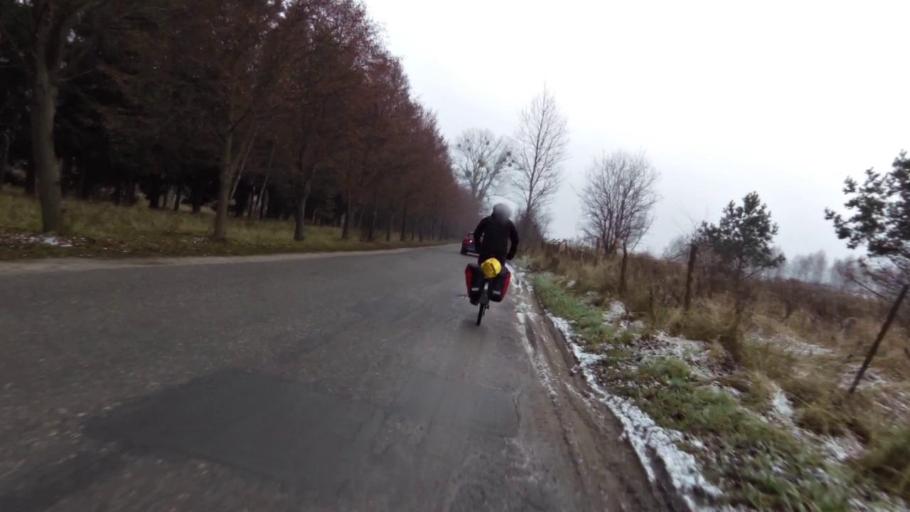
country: PL
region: West Pomeranian Voivodeship
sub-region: Powiat walecki
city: Walcz
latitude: 53.2860
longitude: 16.4736
